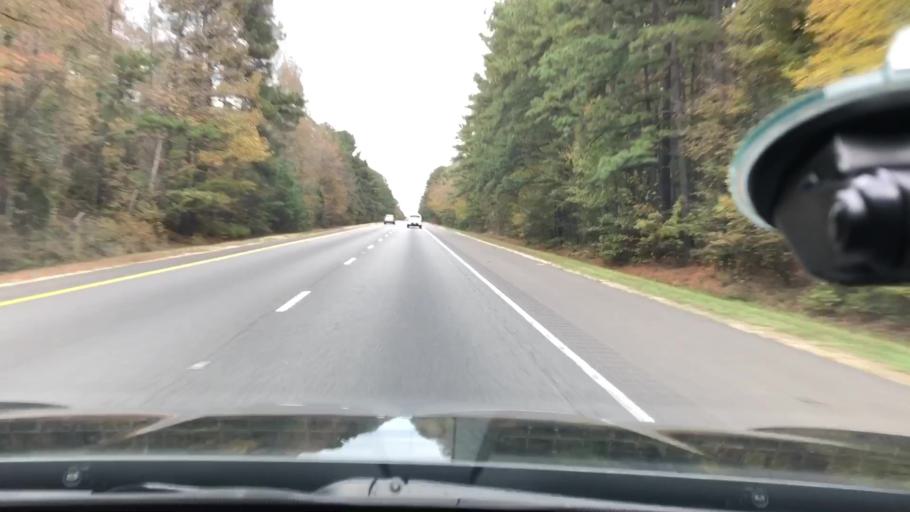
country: US
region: Arkansas
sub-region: Hot Spring County
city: Malvern
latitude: 34.2915
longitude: -92.9516
